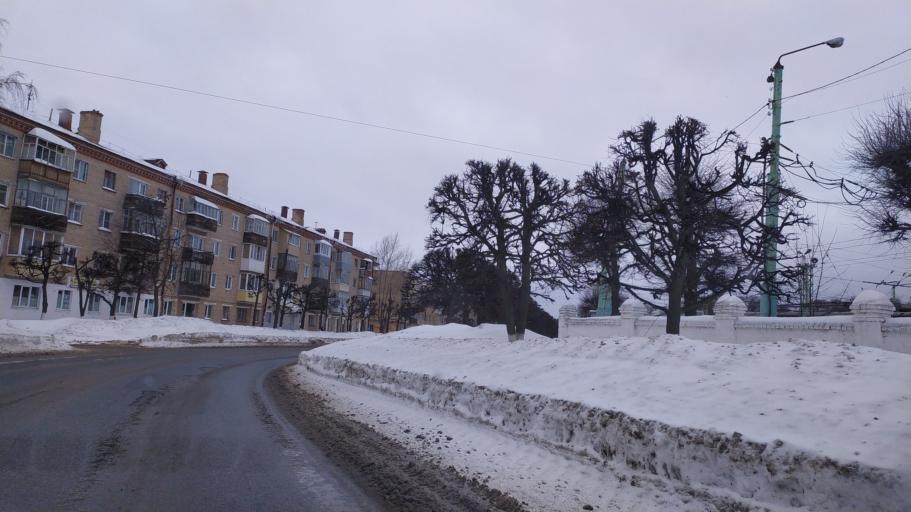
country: RU
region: Chuvashia
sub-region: Cheboksarskiy Rayon
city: Cheboksary
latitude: 56.1161
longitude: 47.2635
